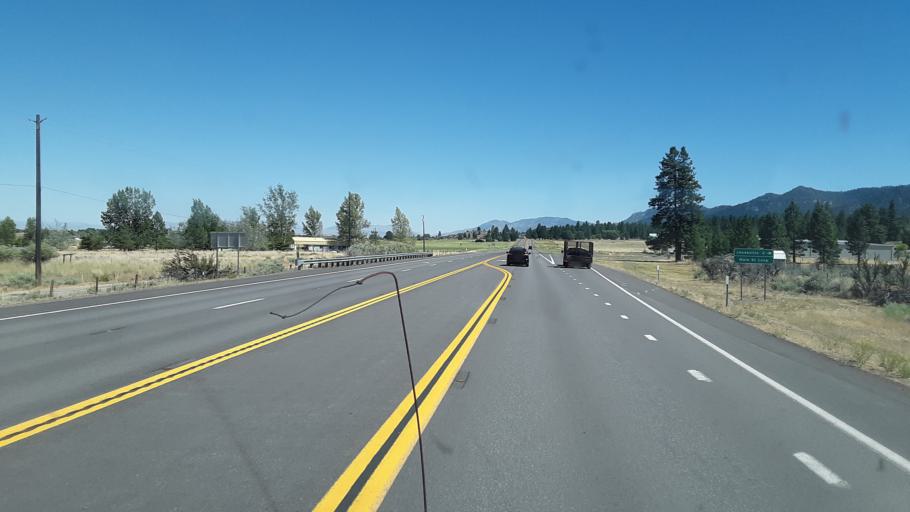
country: US
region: California
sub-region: Lassen County
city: Janesville
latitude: 40.3154
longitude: -120.5401
